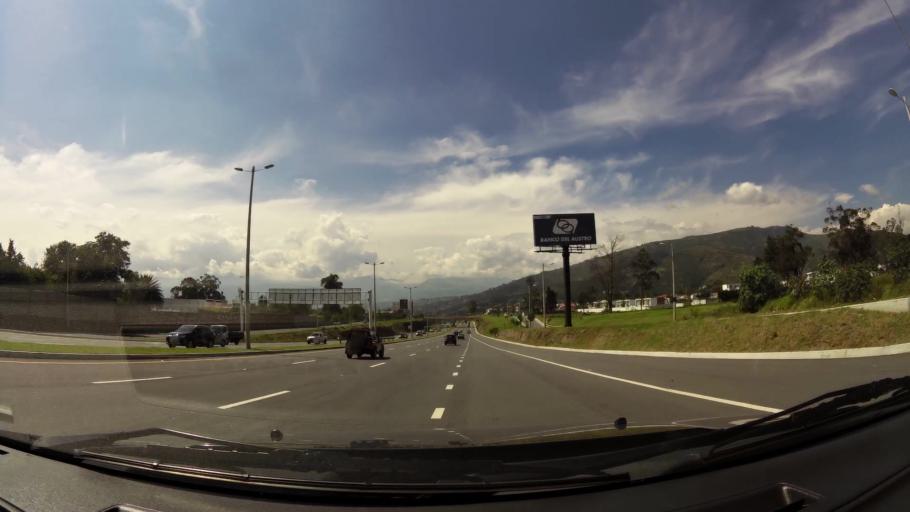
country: EC
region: Pichincha
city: Quito
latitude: -0.2162
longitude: -78.4399
